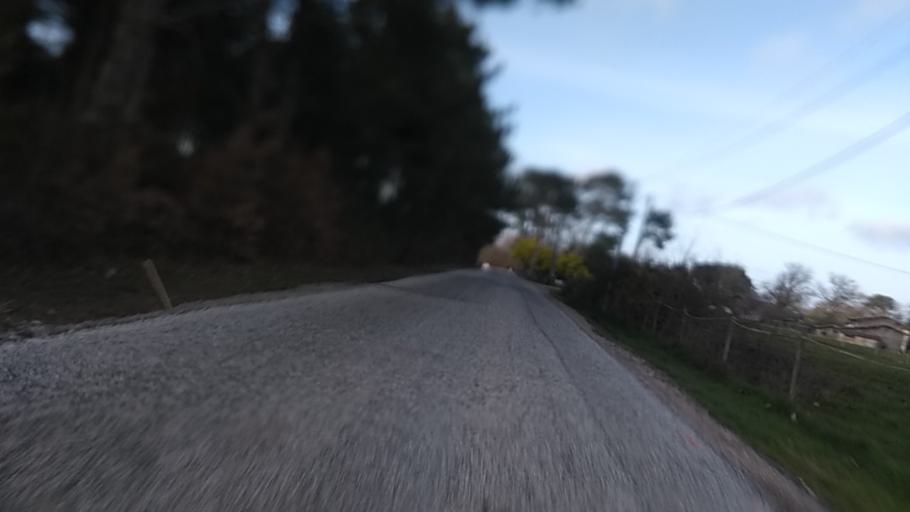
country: FR
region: Aquitaine
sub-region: Departement de la Gironde
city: Le Barp
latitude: 44.5797
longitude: -0.7710
